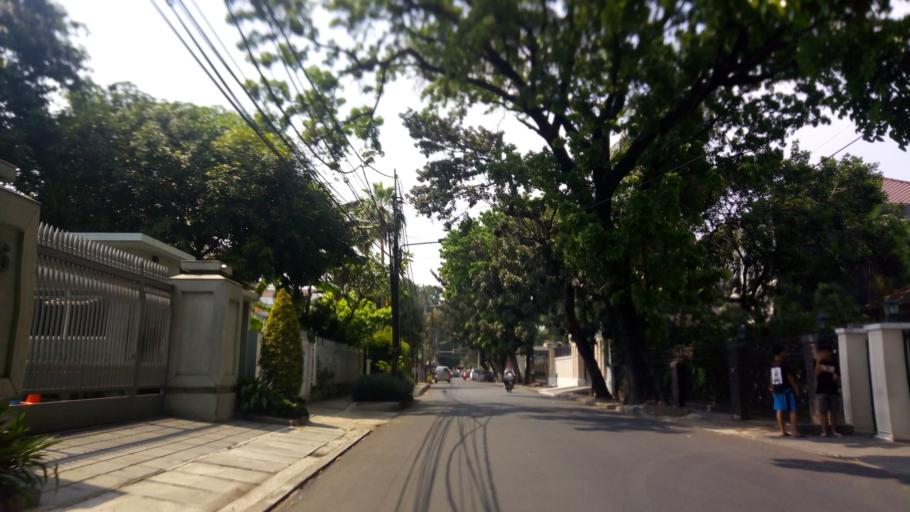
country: ID
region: Jakarta Raya
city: Jakarta
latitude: -6.2010
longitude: 106.8299
